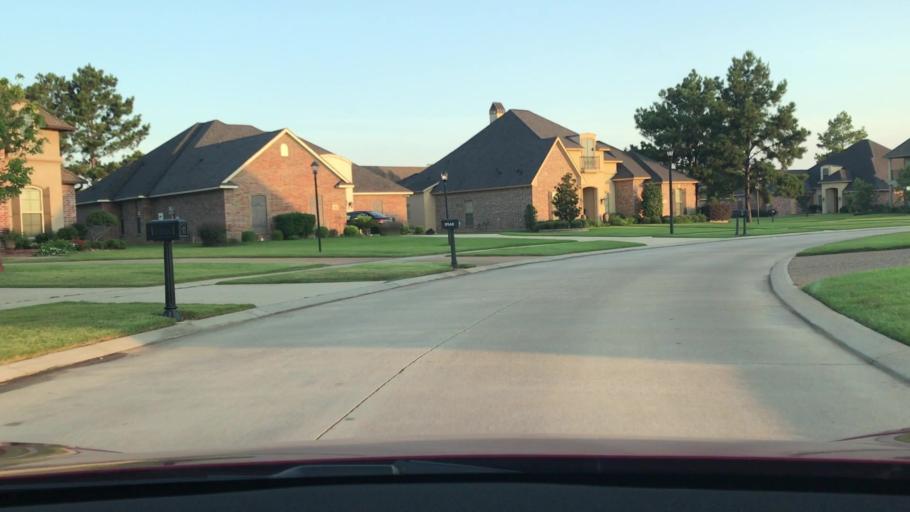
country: US
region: Louisiana
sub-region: Bossier Parish
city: Bossier City
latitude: 32.3936
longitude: -93.7047
